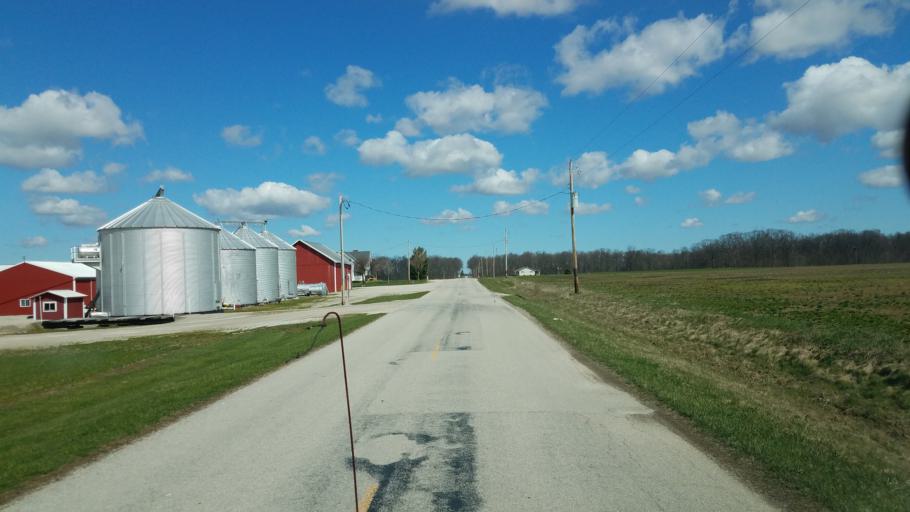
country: US
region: Ohio
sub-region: Sandusky County
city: Mount Carmel
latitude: 41.1766
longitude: -82.9381
